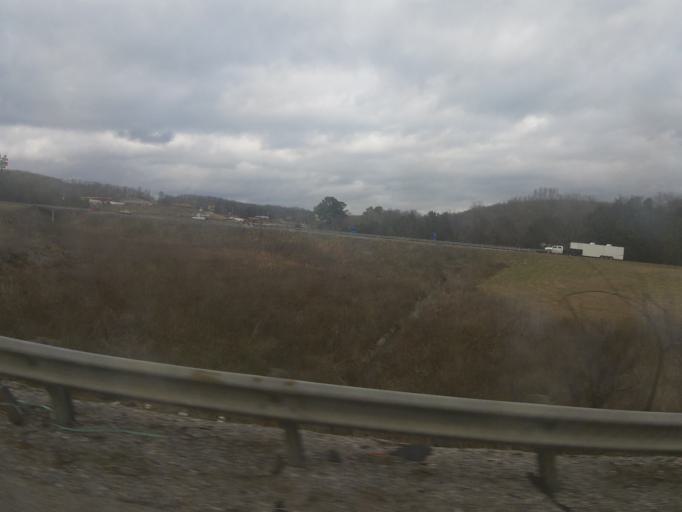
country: US
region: Tennessee
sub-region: Marion County
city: Jasper
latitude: 35.0316
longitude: -85.5807
